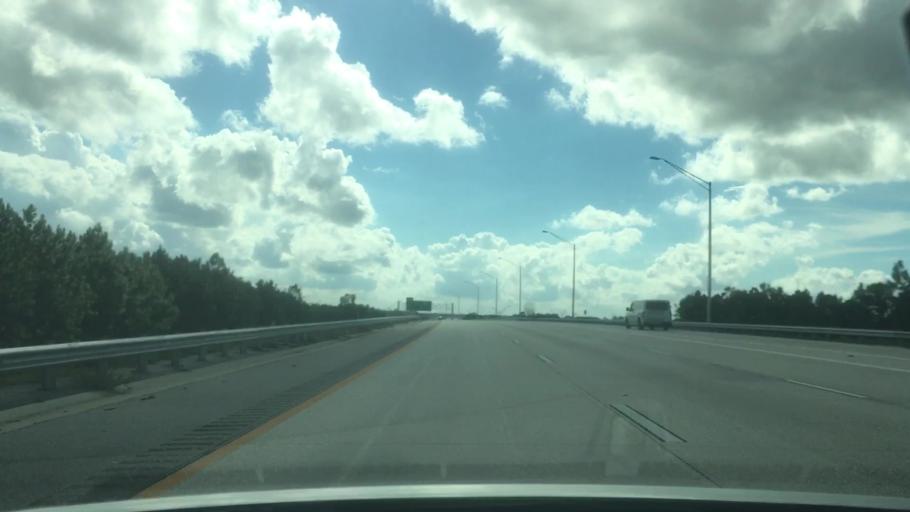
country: US
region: Florida
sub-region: Saint Johns County
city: Fruit Cove
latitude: 30.1175
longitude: -81.5140
